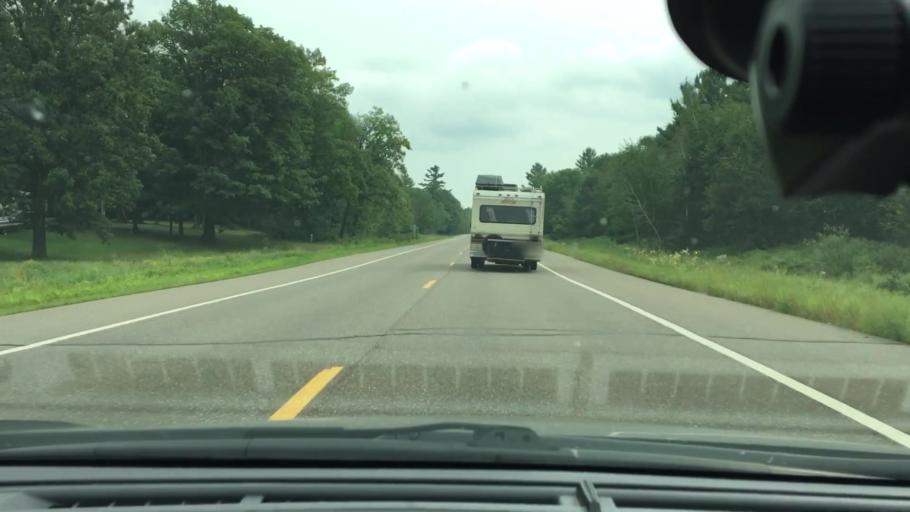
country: US
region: Minnesota
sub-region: Crow Wing County
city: Crosby
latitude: 46.4105
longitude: -93.8560
